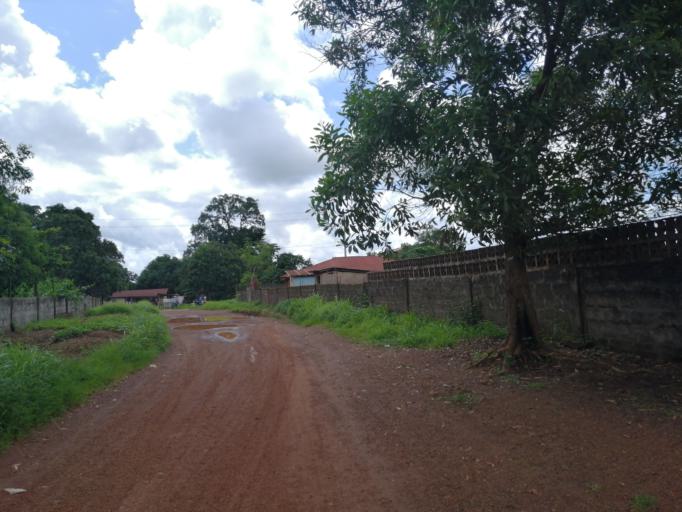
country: SL
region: Northern Province
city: Port Loko
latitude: 8.7675
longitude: -12.7816
